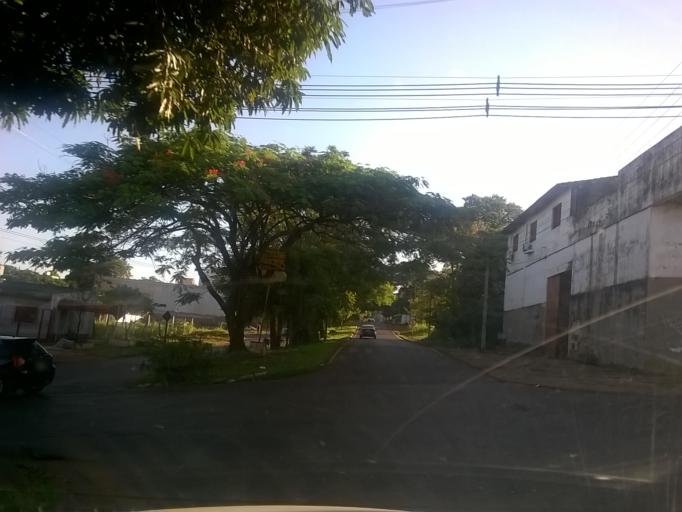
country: PY
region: Alto Parana
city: Ciudad del Este
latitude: -25.5041
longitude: -54.6288
